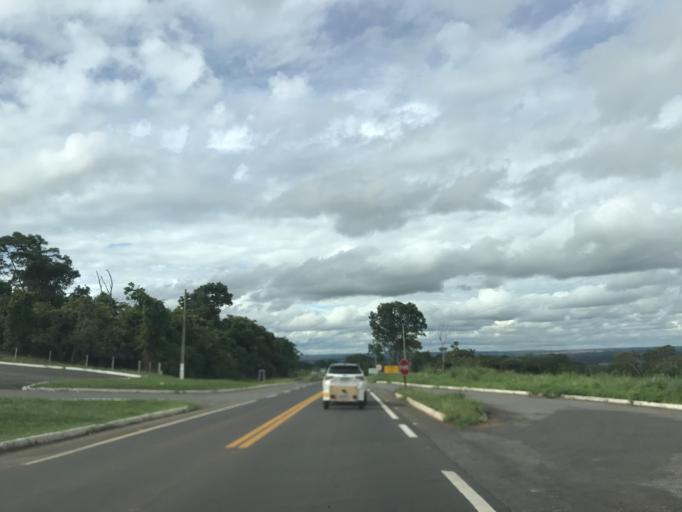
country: BR
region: Goias
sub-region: Piracanjuba
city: Piracanjuba
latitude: -17.2143
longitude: -48.7091
